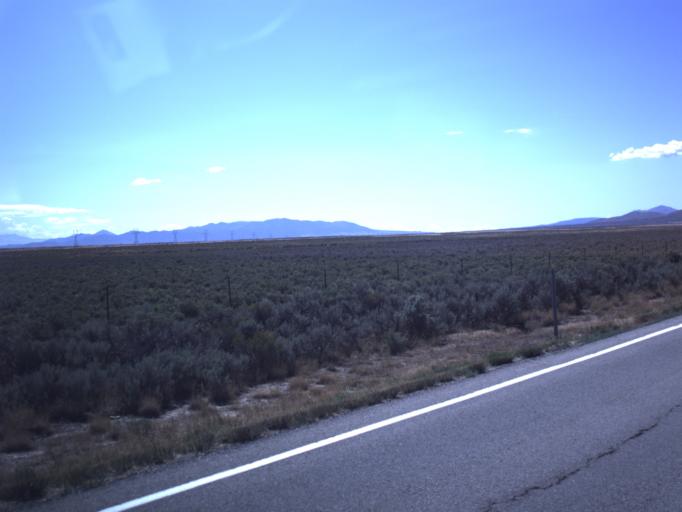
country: US
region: Utah
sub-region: Tooele County
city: Tooele
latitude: 40.2427
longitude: -112.4010
